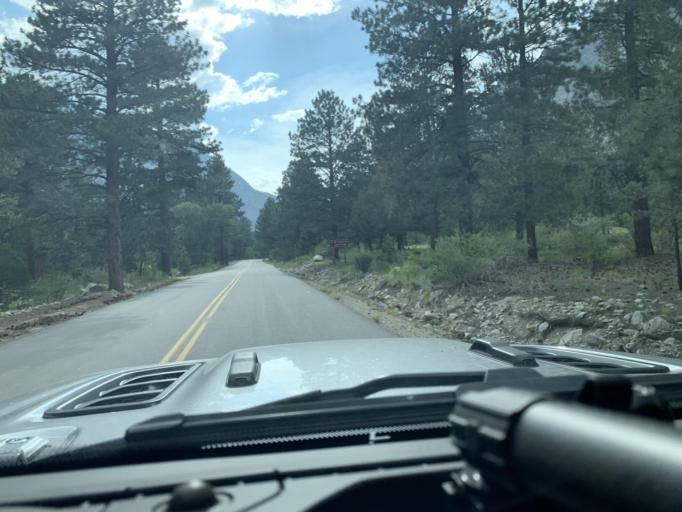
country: US
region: Colorado
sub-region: Chaffee County
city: Buena Vista
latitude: 38.7143
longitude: -106.2245
